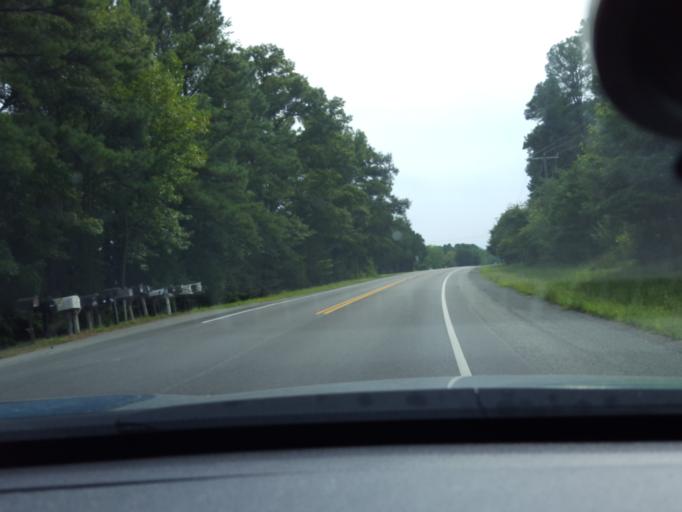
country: US
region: Virginia
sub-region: Hanover County
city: Hanover
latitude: 37.7323
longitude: -77.3602
